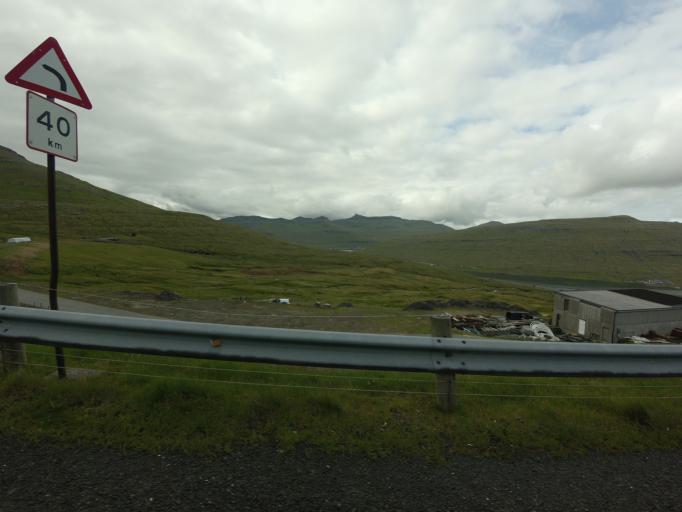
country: FO
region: Streymoy
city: Kollafjordhur
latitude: 62.2206
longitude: -6.9832
